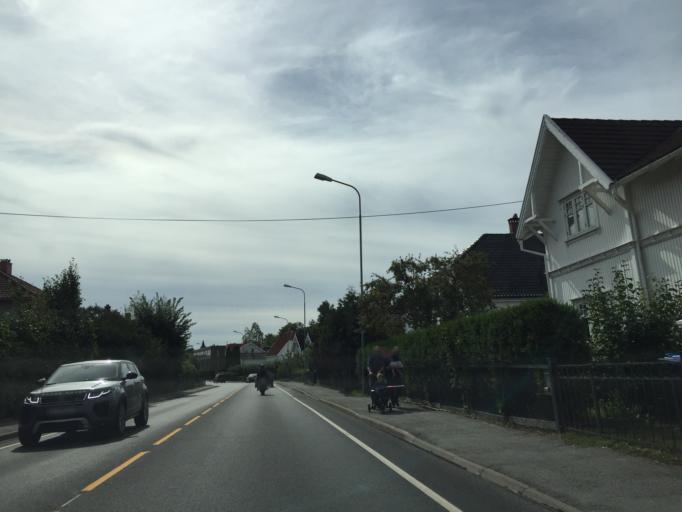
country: NO
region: Ostfold
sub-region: Fredrikstad
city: Fredrikstad
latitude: 59.2031
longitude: 10.9384
